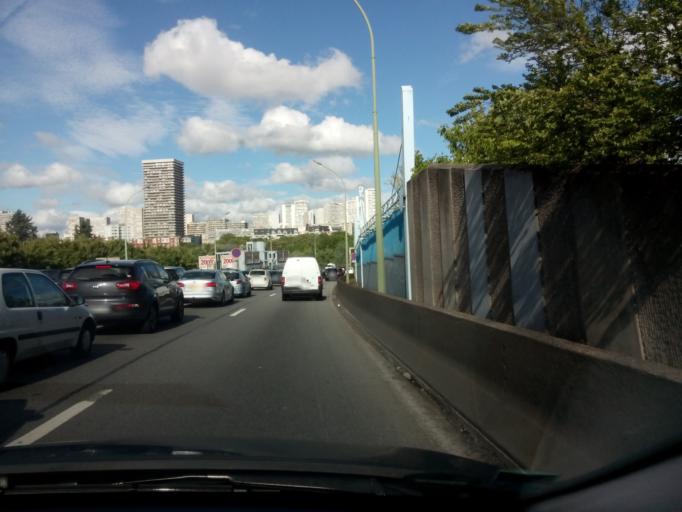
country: FR
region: Ile-de-France
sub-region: Departement du Val-de-Marne
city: Gentilly
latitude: 48.8175
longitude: 2.3502
